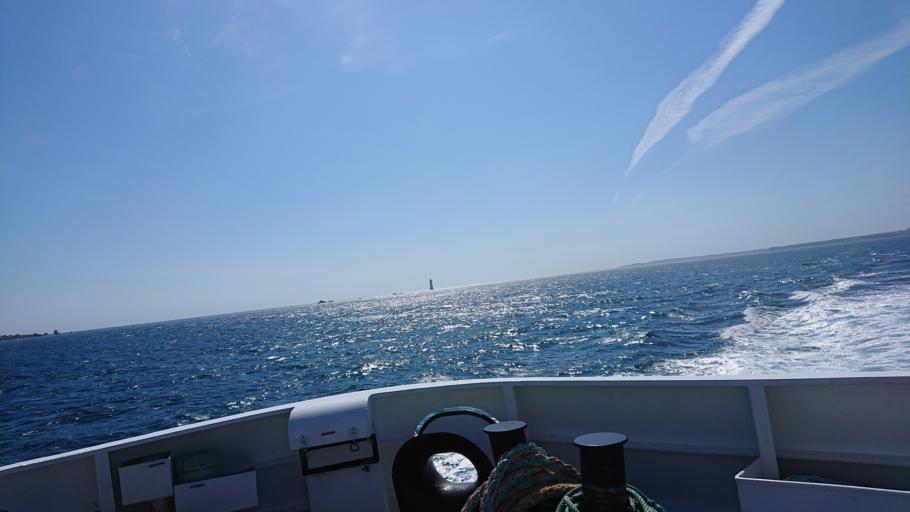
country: FR
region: Brittany
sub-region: Departement du Finistere
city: Porspoder
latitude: 48.4461
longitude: -4.9976
